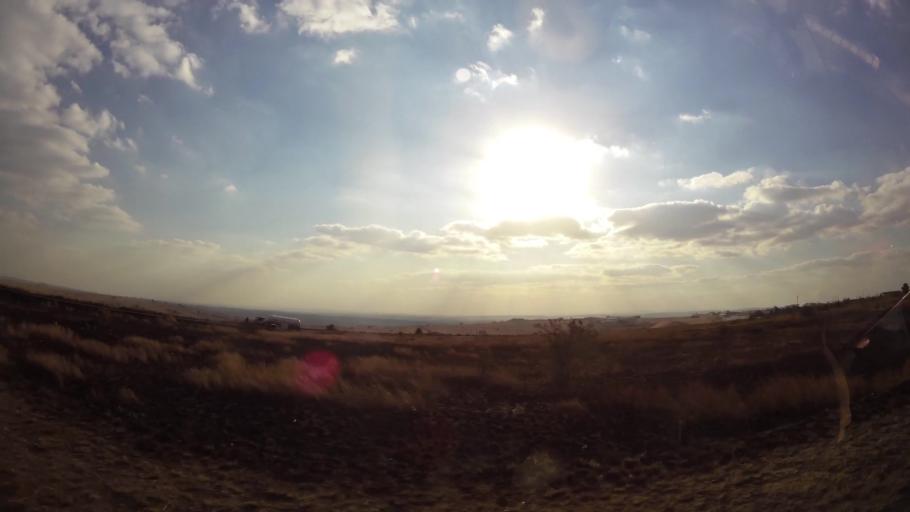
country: ZA
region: Gauteng
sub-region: West Rand District Municipality
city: Krugersdorp
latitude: -26.0903
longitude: 27.7336
